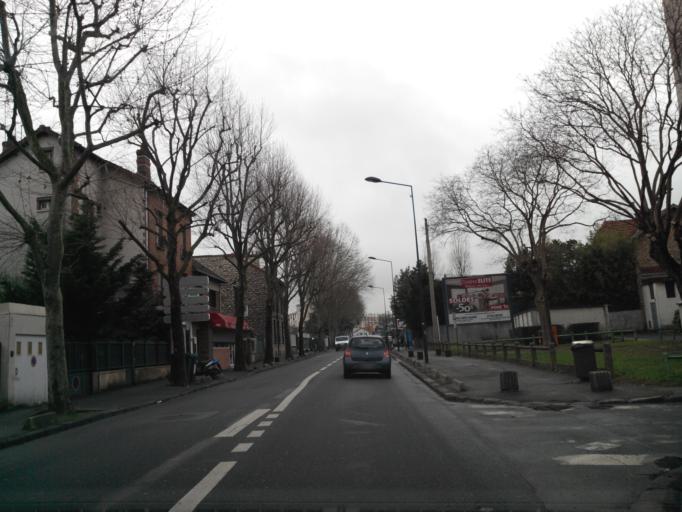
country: FR
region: Ile-de-France
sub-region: Departement du Val-de-Marne
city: Villejuif
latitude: 48.7873
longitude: 2.3536
